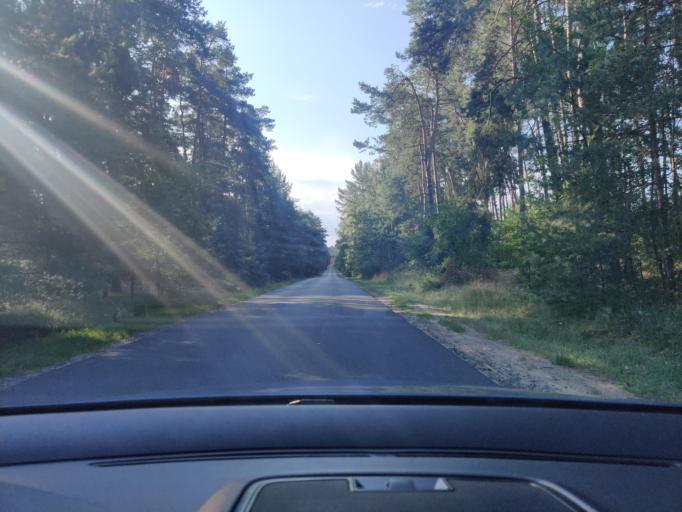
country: PL
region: Greater Poland Voivodeship
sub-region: Konin
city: Konin
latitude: 52.1809
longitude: 18.3338
